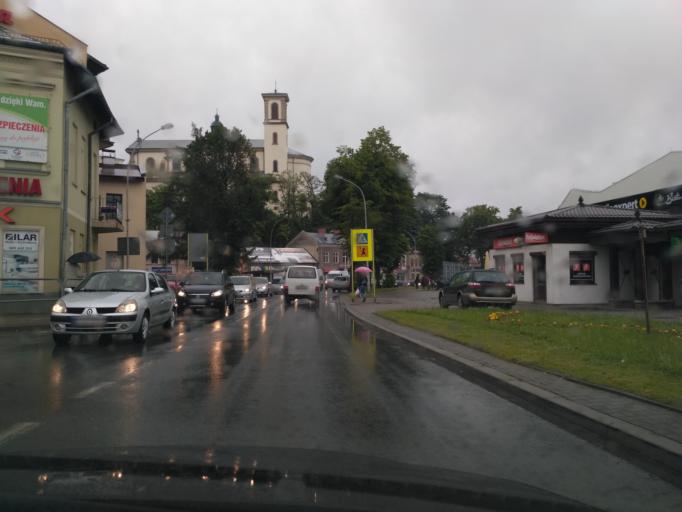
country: PL
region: Lesser Poland Voivodeship
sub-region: Powiat gorlicki
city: Gorlice
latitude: 49.6564
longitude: 21.1592
